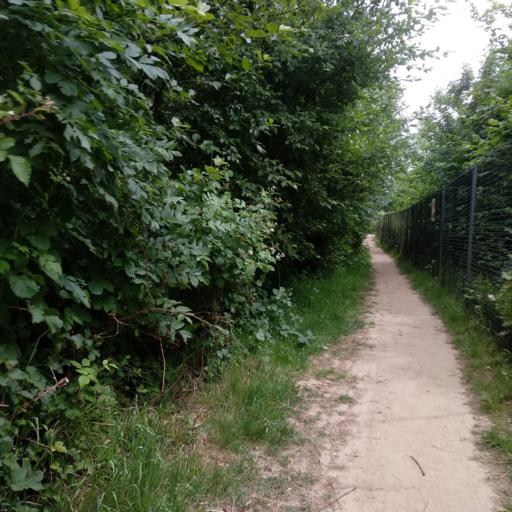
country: GB
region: England
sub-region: Kent
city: Ashford
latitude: 51.1589
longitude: 0.8476
